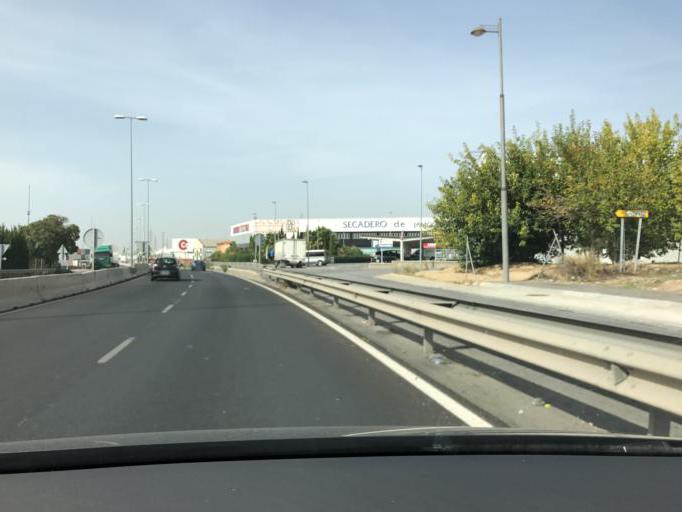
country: ES
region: Andalusia
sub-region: Provincia de Granada
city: Maracena
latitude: 37.2043
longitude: -3.6559
